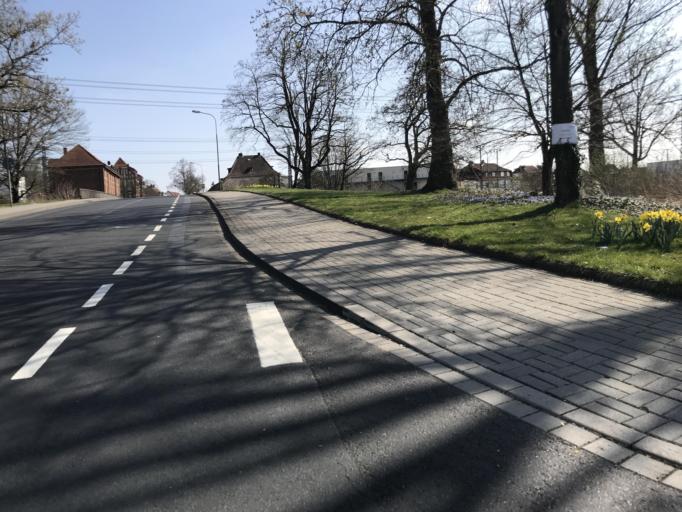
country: DE
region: Hesse
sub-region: Regierungsbezirk Kassel
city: Fulda
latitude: 50.5637
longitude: 9.6796
